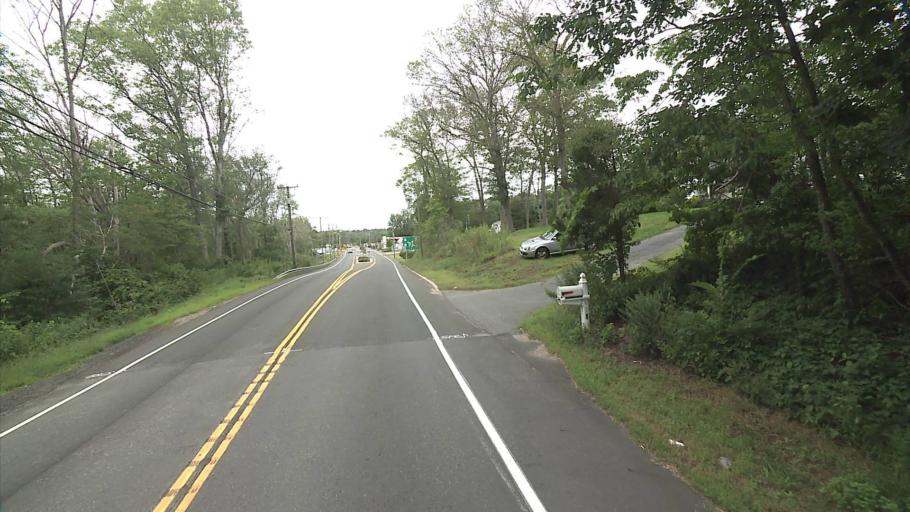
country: US
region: Connecticut
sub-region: New London County
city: Montville Center
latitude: 41.4746
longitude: -72.2620
